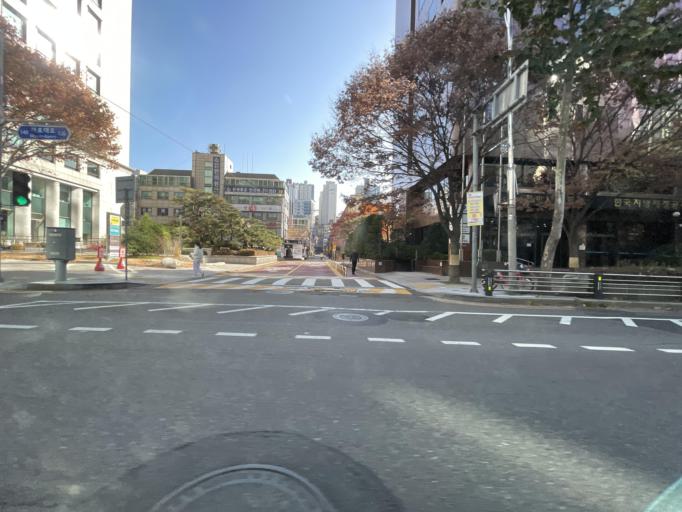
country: KR
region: Seoul
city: Seoul
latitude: 37.5467
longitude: 126.9532
